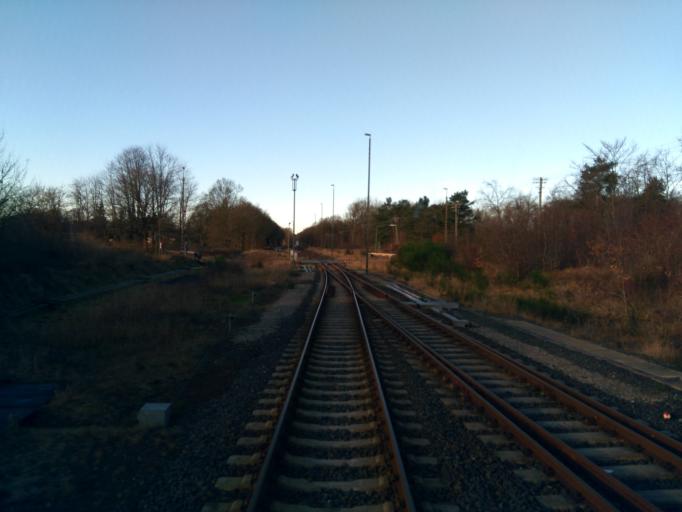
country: DE
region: Lower Saxony
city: Munster
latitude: 52.9943
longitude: 10.0911
